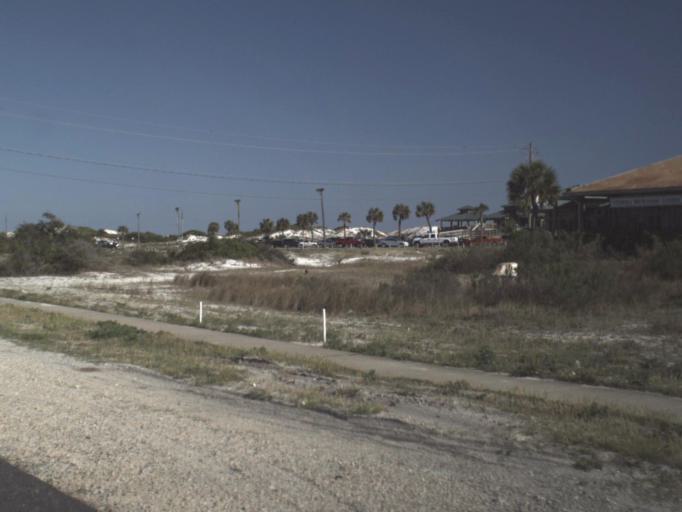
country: US
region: Florida
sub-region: Okaloosa County
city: Fort Walton Beach
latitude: 30.3955
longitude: -86.5855
